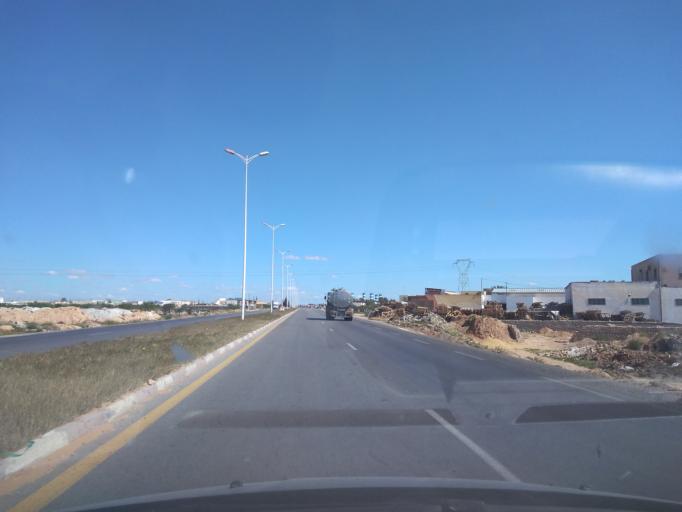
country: TN
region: Safaqis
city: Sfax
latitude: 34.8058
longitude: 10.6909
